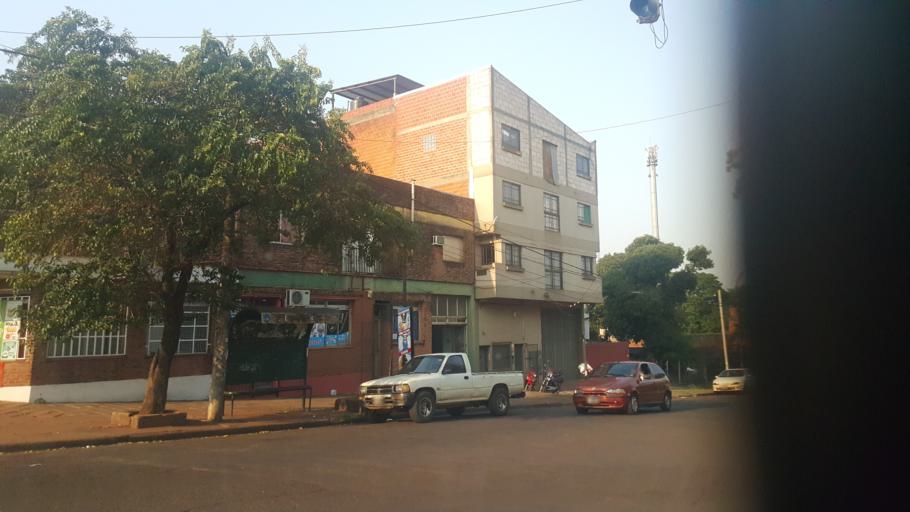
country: AR
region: Misiones
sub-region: Departamento de Capital
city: Posadas
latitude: -27.3936
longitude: -55.9088
